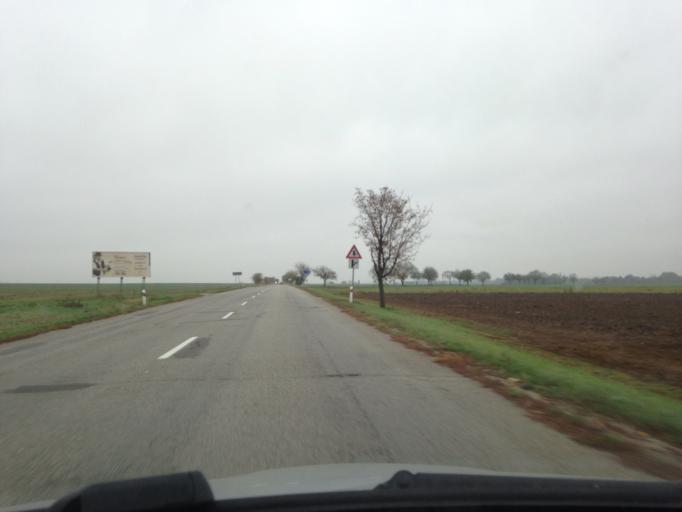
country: SK
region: Nitriansky
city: Svodin
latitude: 47.8844
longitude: 18.4210
